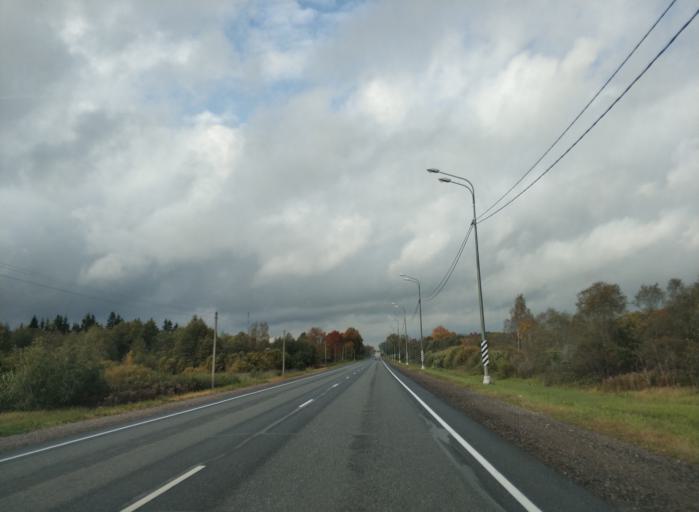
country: RU
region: Pskov
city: Ostrov
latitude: 57.1215
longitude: 28.5266
